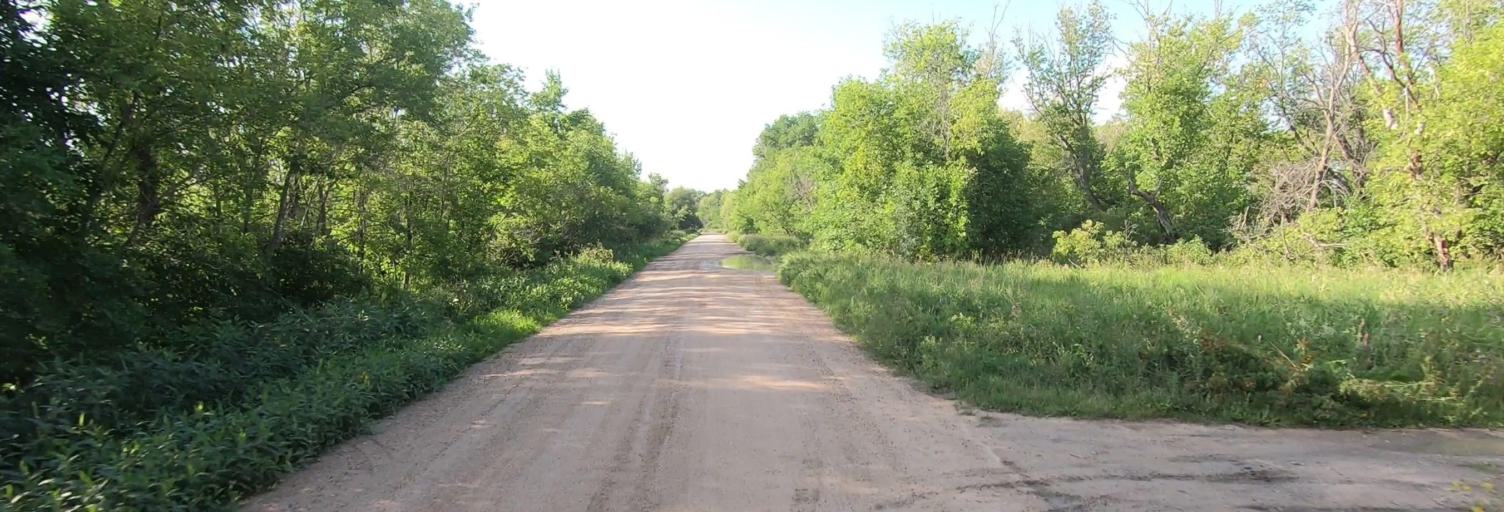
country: CA
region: Manitoba
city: Selkirk
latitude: 50.2769
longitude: -96.8517
